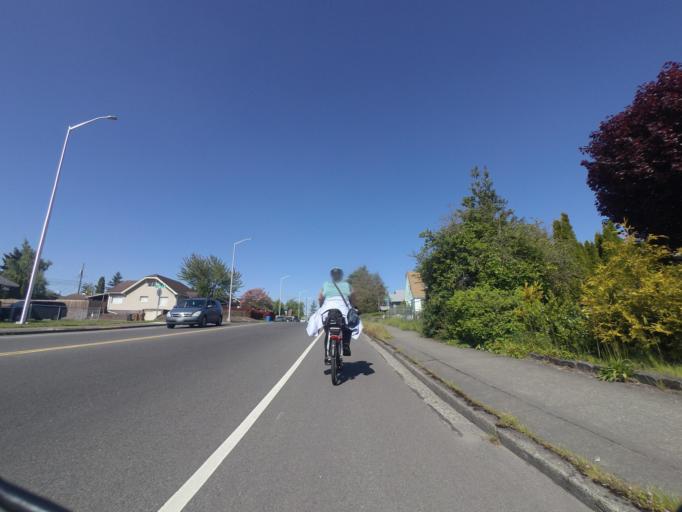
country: US
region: Washington
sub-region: Pierce County
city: Tacoma
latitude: 47.2065
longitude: -122.4376
